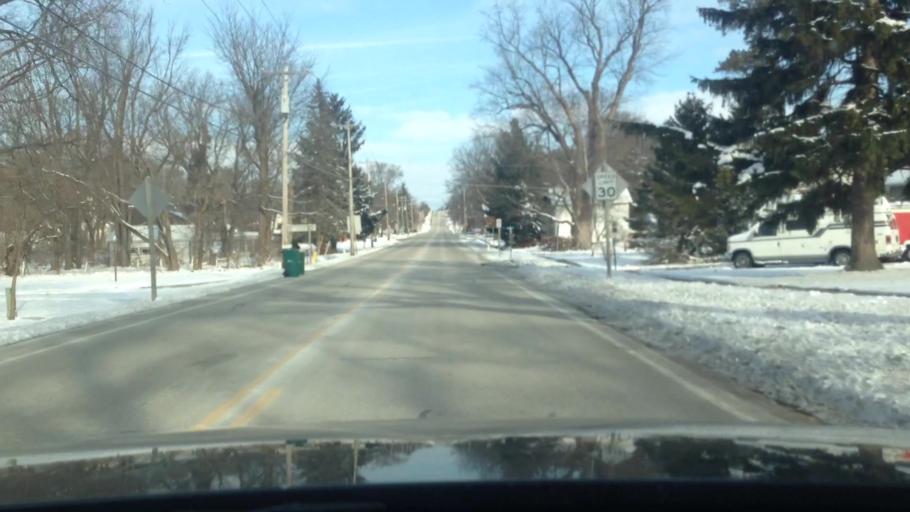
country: US
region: Wisconsin
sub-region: Walworth County
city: Lake Geneva
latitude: 42.6410
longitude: -88.4136
